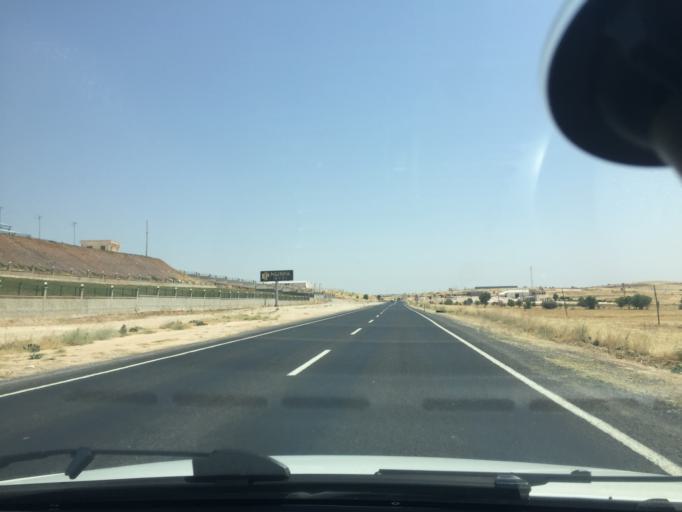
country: TR
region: Mardin
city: Kindirip
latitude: 37.4571
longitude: 41.2432
